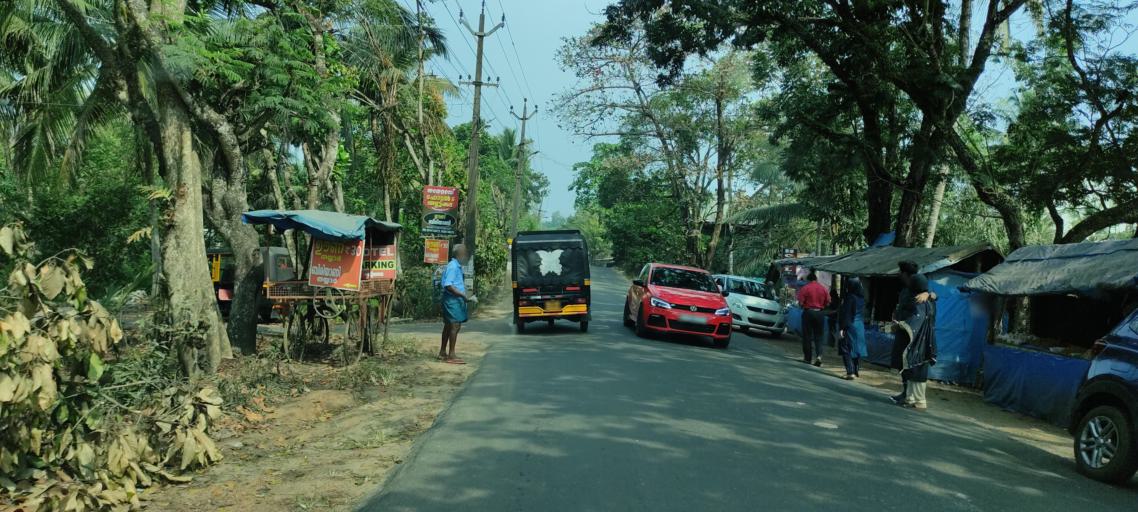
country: IN
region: Kerala
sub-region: Alappuzha
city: Shertallai
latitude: 9.6727
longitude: 76.4175
